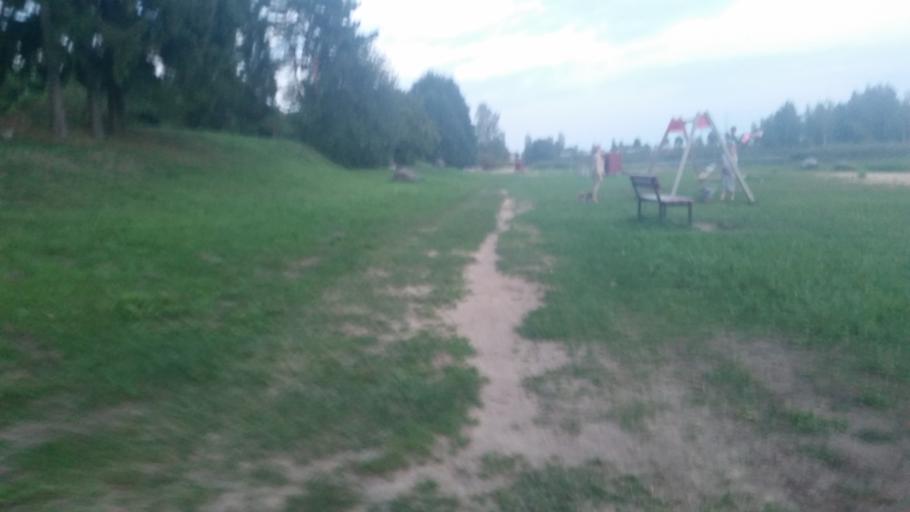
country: LV
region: Ogre
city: Ogre
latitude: 56.8141
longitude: 24.5924
